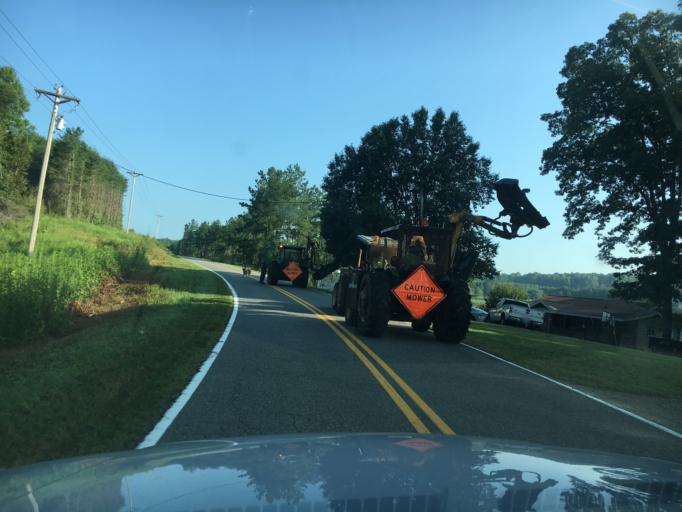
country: US
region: North Carolina
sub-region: Rutherford County
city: Rutherfordton
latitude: 35.2645
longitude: -82.0304
